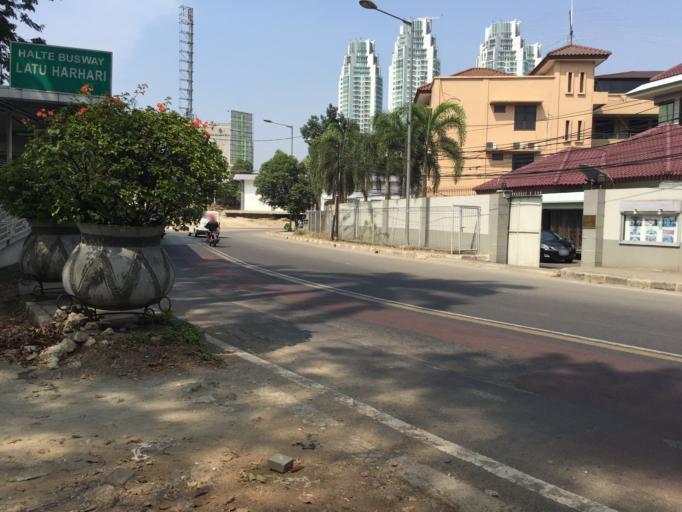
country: ID
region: Jakarta Raya
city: Jakarta
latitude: -6.2027
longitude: 106.8275
